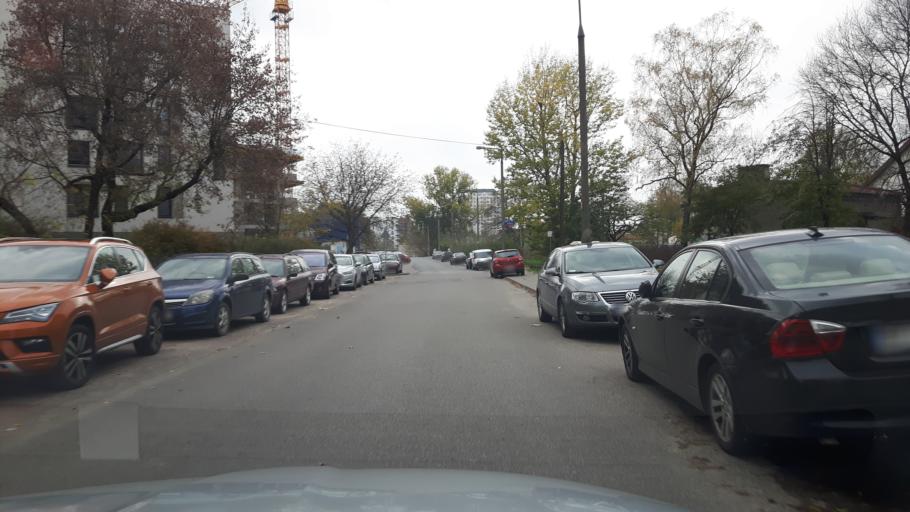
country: PL
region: Masovian Voivodeship
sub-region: Warszawa
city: Praga Polnoc
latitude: 52.2689
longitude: 21.0462
